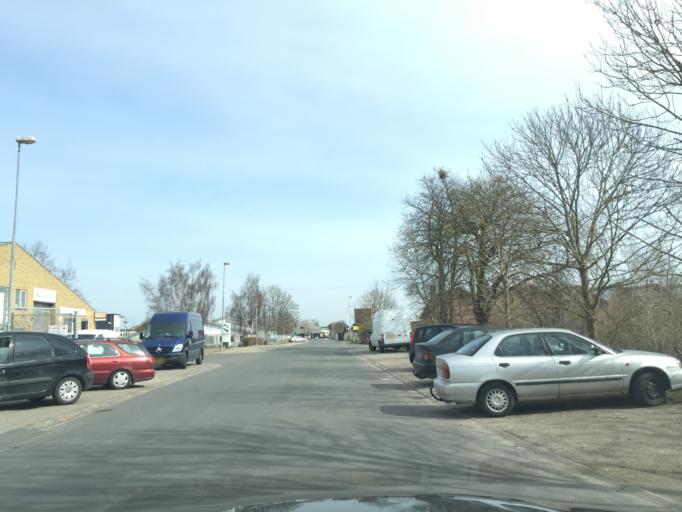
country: DK
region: South Denmark
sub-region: Odense Kommune
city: Odense
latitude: 55.3922
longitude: 10.3594
